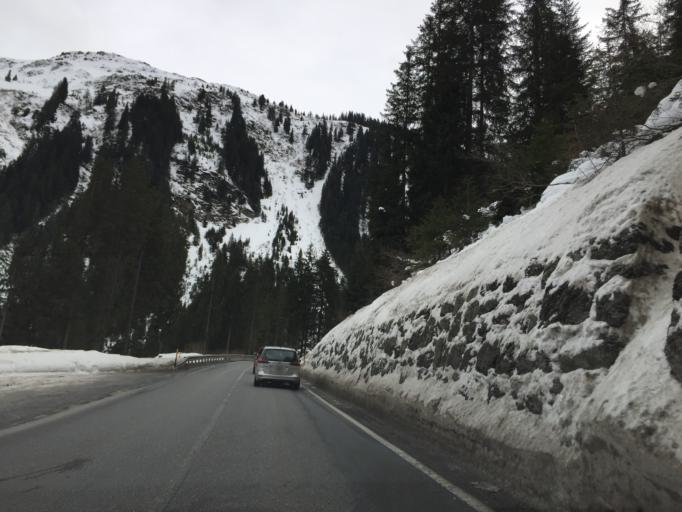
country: CH
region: Grisons
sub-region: Praettigau/Davos District
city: Klosters Serneus
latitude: 46.8486
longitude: 9.8823
